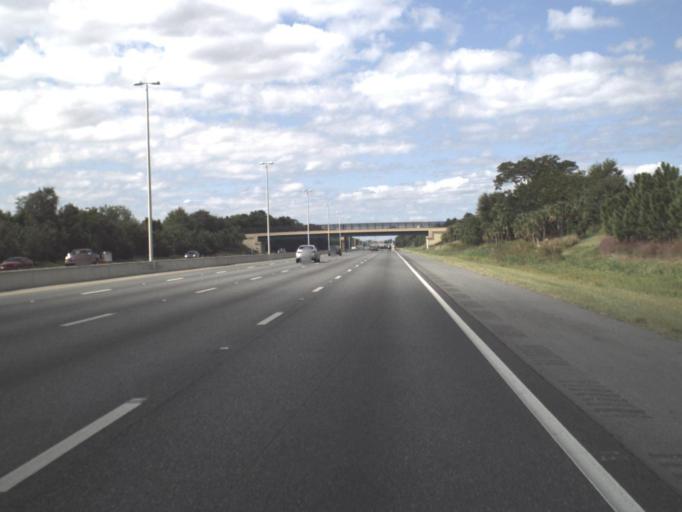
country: US
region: Florida
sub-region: Orange County
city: Winter Garden
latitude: 28.5454
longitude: -81.5840
